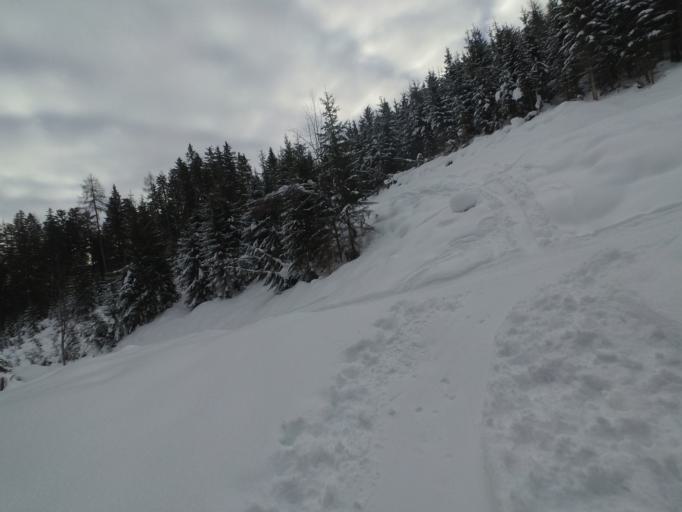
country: AT
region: Salzburg
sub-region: Politischer Bezirk Sankt Johann im Pongau
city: Sankt Johann im Pongau
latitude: 47.3210
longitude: 13.2208
